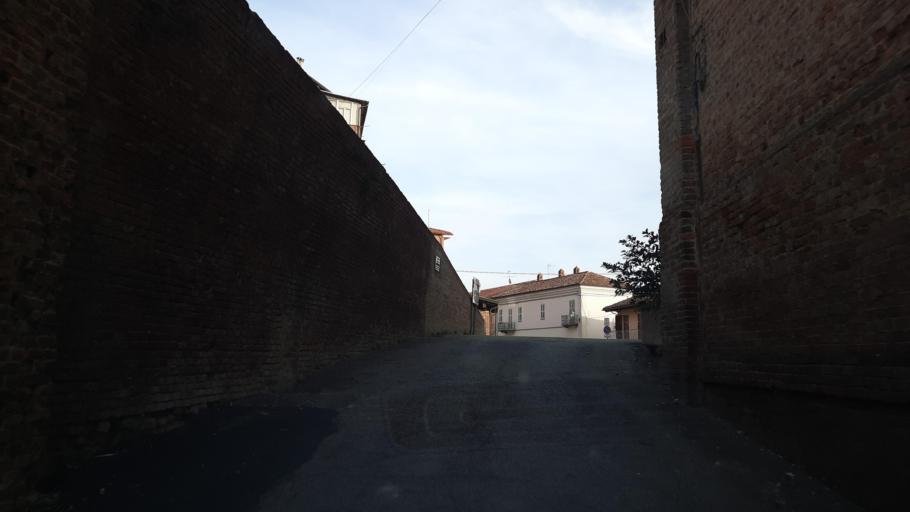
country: IT
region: Piedmont
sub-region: Provincia di Asti
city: Tonco
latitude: 45.0239
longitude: 8.1887
